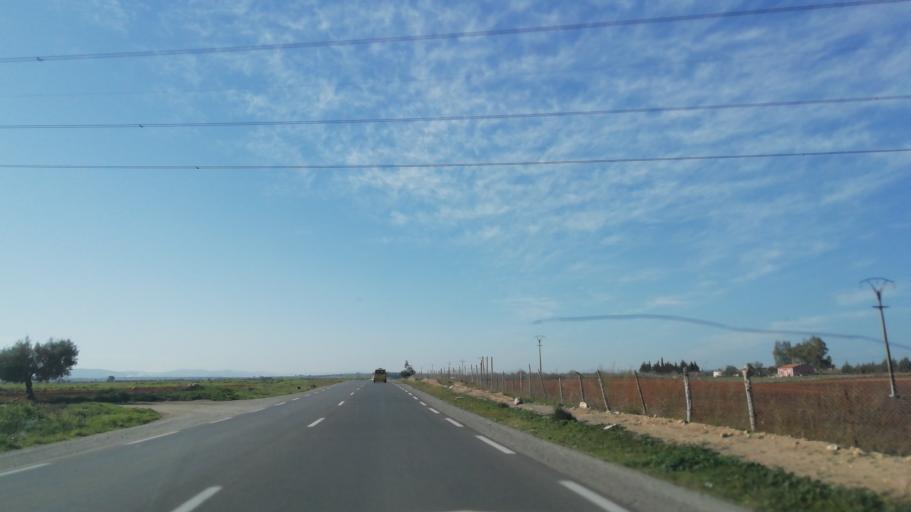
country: DZ
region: Tlemcen
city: Ouled Mimoun
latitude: 35.0415
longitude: -0.8468
